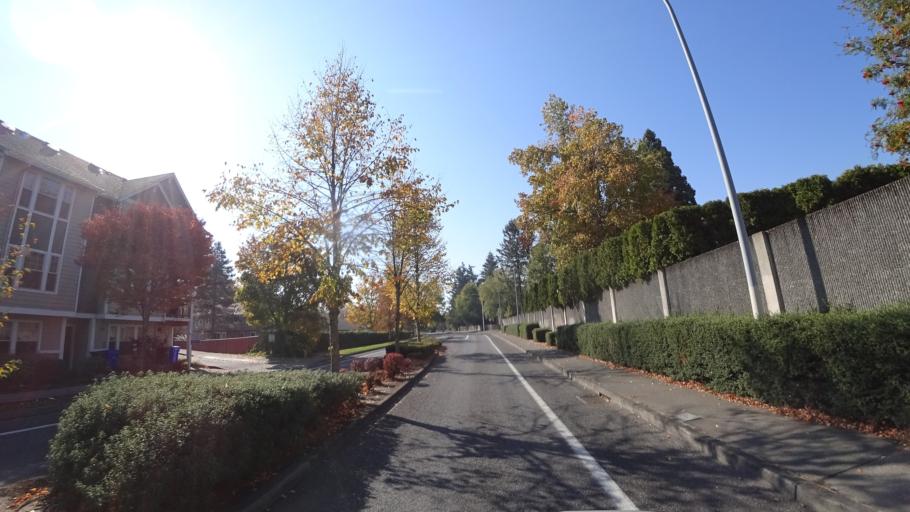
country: US
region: Oregon
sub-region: Multnomah County
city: Gresham
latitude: 45.4940
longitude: -122.4436
